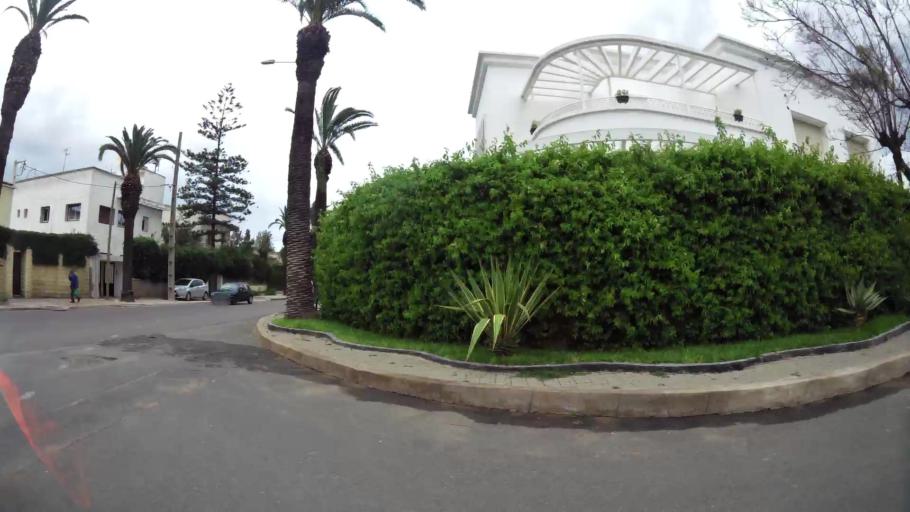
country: MA
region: Grand Casablanca
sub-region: Casablanca
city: Casablanca
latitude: 33.5554
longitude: -7.6176
